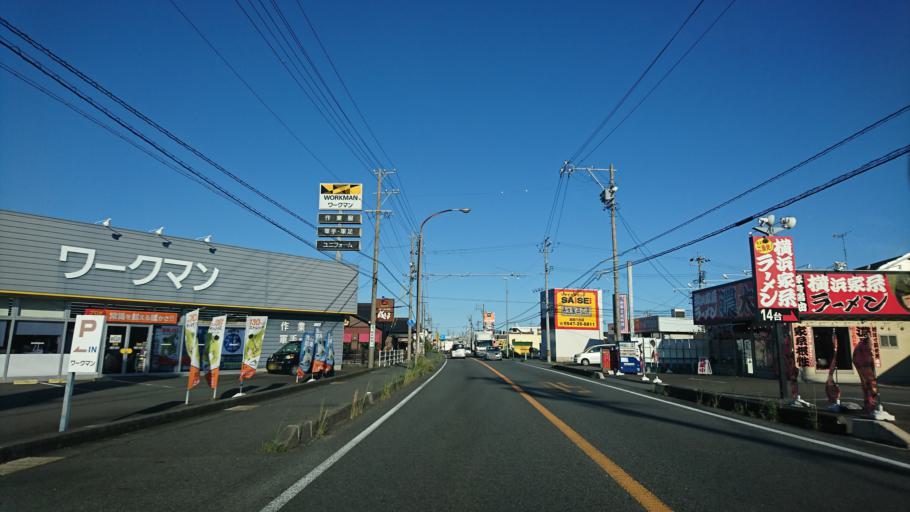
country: JP
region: Shizuoka
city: Shimada
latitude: 34.8369
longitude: 138.2018
